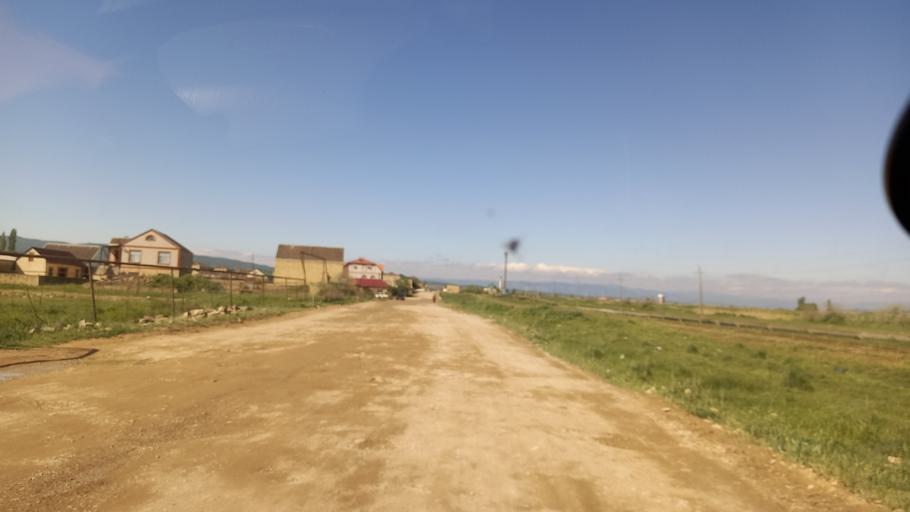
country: RU
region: Dagestan
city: Dagestanskiye Ogni
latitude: 42.1278
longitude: 48.2206
